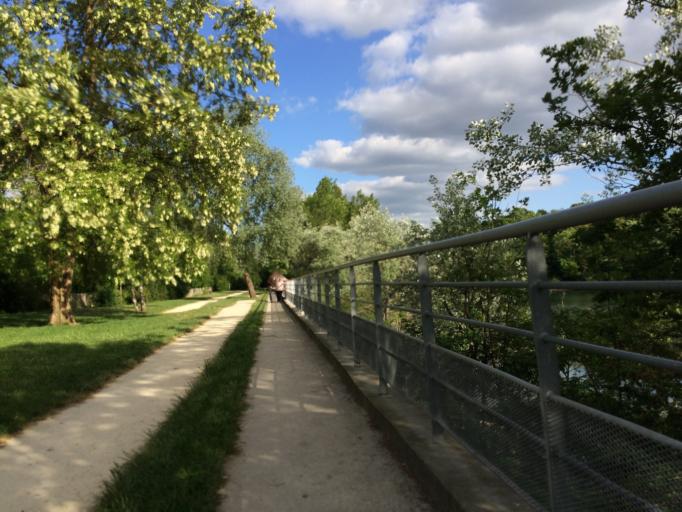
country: FR
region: Ile-de-France
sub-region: Departement de l'Essonne
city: Ris-Orangis
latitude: 48.6567
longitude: 2.4201
